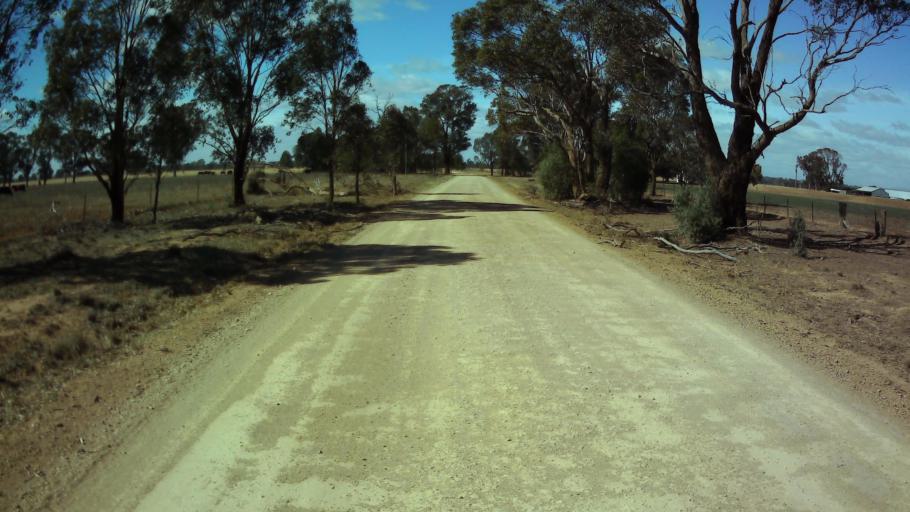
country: AU
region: New South Wales
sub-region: Weddin
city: Grenfell
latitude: -34.0278
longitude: 148.3178
